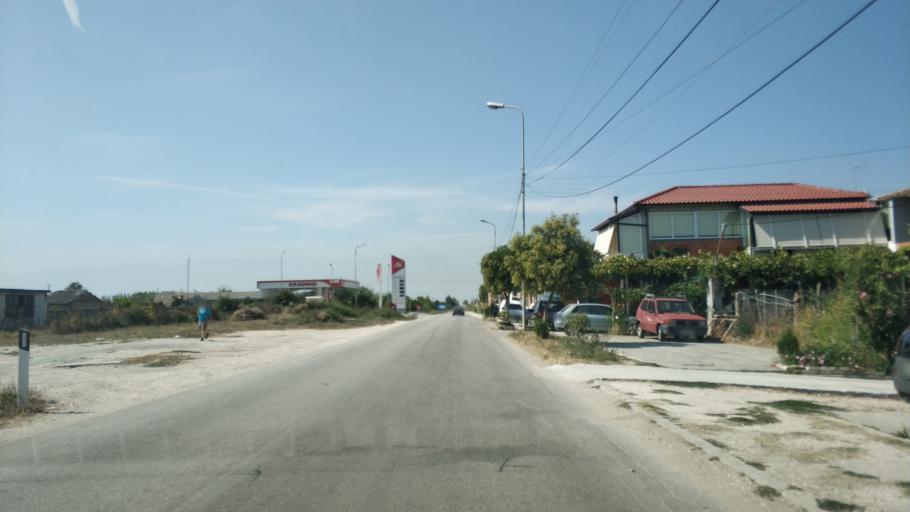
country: AL
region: Fier
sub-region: Rrethi i Fierit
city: Dermenas
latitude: 40.7376
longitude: 19.5180
